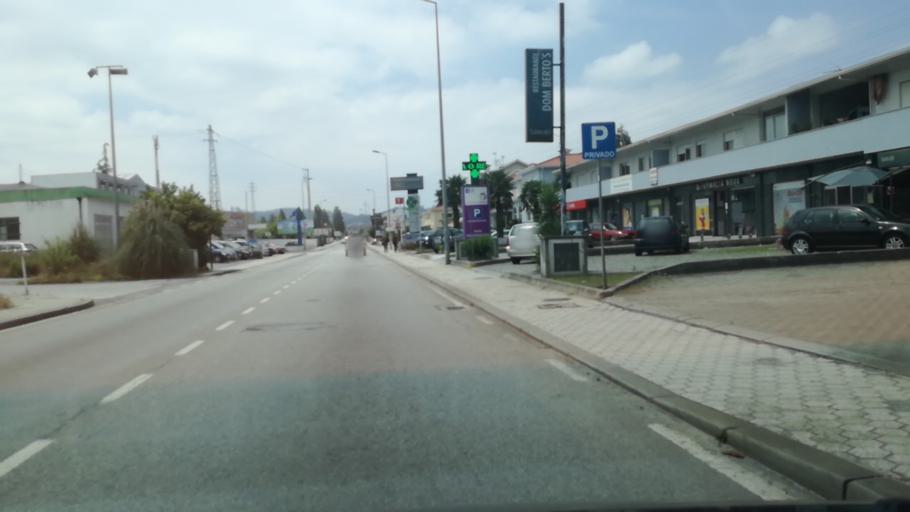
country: PT
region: Porto
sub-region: Trofa
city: Bougado
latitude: 41.3297
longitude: -8.5655
